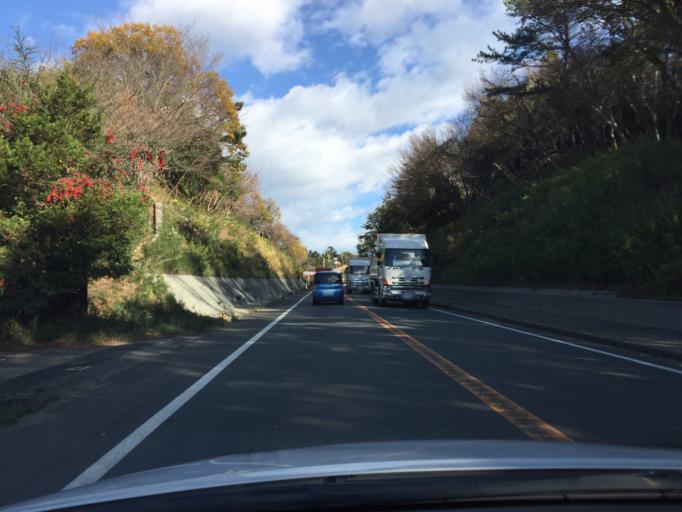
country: JP
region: Fukushima
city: Namie
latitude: 37.3293
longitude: 141.0166
